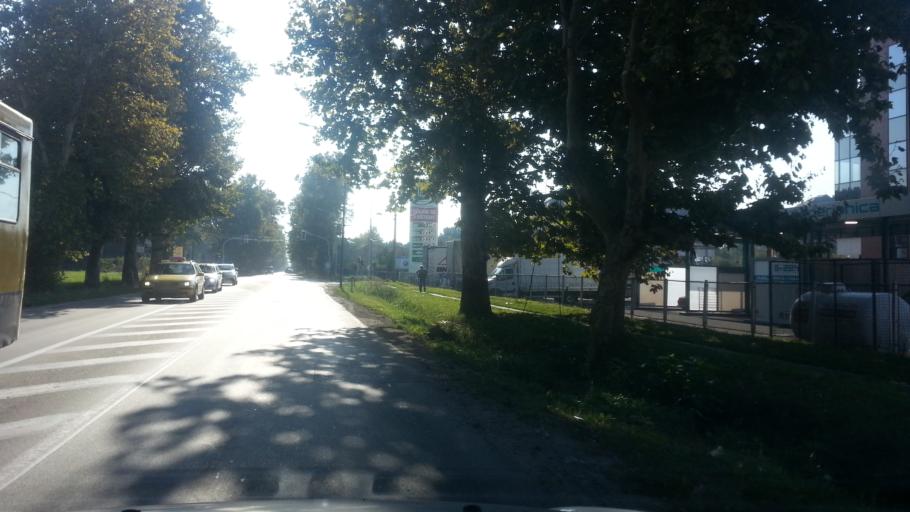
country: RS
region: Central Serbia
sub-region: Belgrade
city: Zemun
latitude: 44.8636
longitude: 20.3676
